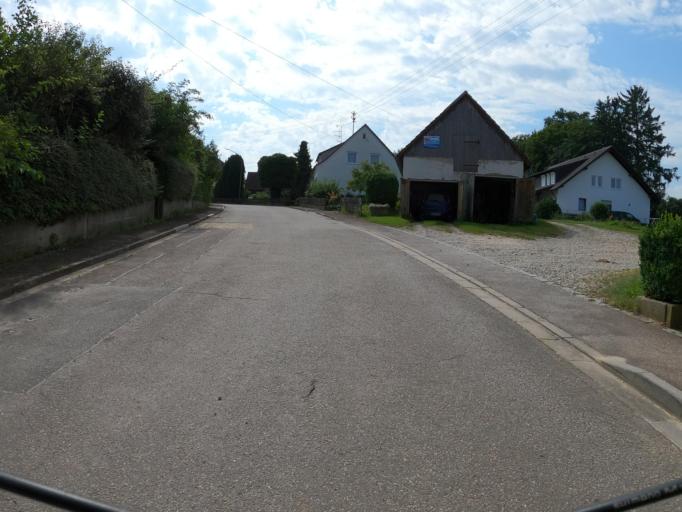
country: DE
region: Bavaria
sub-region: Swabia
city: Rieden an der Kotz
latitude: 48.3812
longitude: 10.2115
